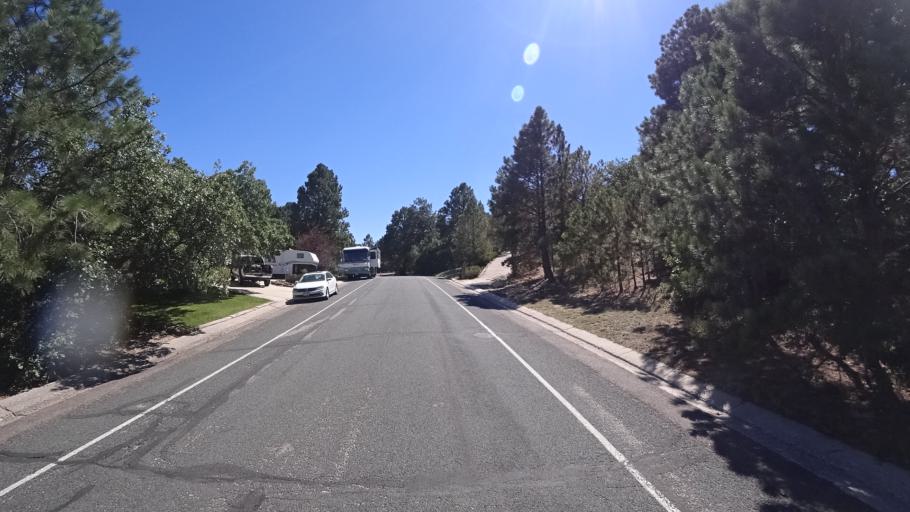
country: US
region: Colorado
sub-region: El Paso County
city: Colorado Springs
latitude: 38.9224
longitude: -104.8004
